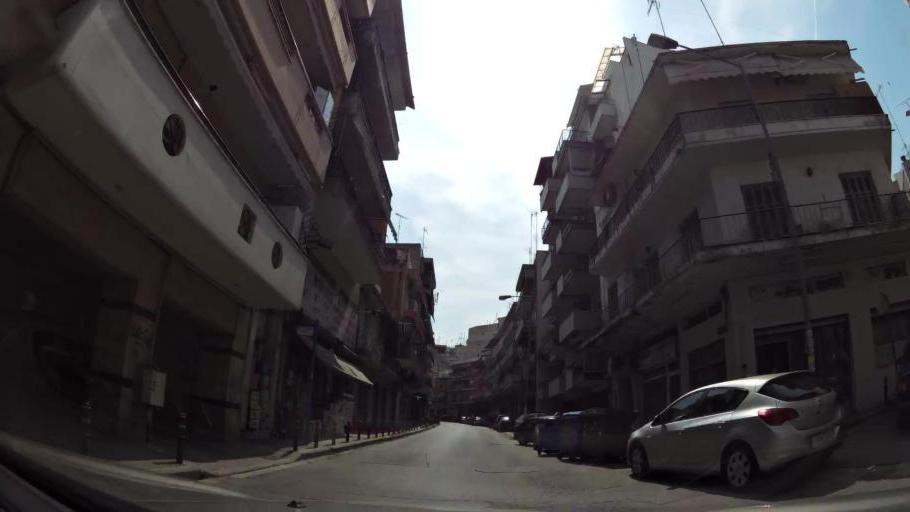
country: GR
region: Central Macedonia
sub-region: Nomos Thessalonikis
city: Sykies
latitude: 40.6499
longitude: 22.9405
